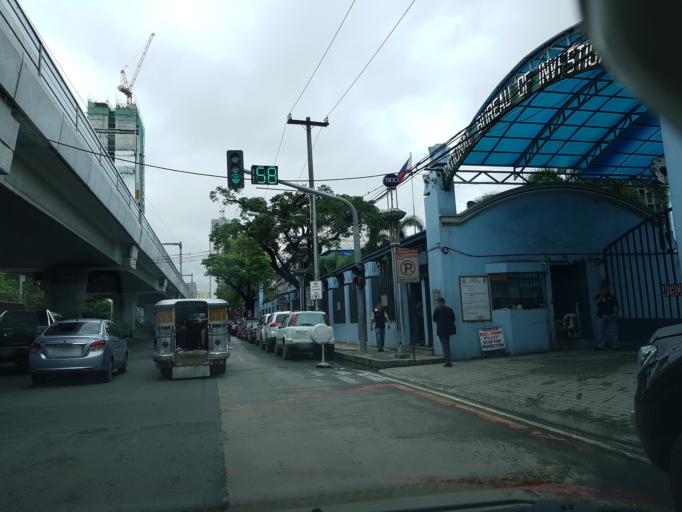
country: PH
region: Metro Manila
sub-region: City of Manila
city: Port Area
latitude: 14.5815
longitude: 120.9851
